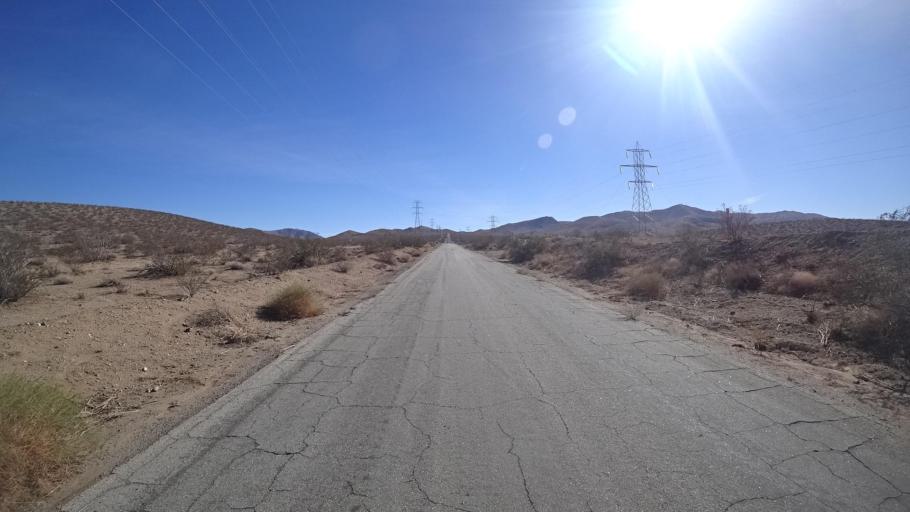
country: US
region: California
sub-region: Kern County
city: Ridgecrest
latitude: 35.3952
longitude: -117.6717
